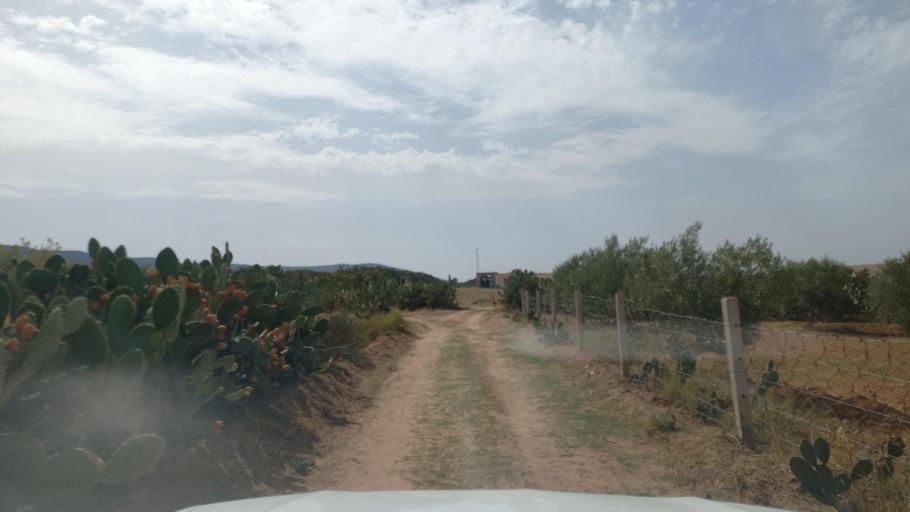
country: TN
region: Al Qasrayn
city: Kasserine
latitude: 35.3533
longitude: 8.8726
